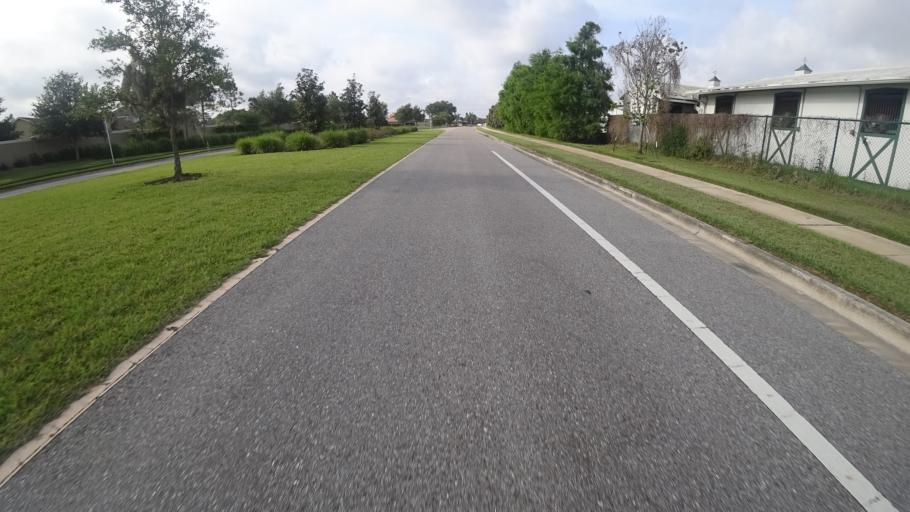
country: US
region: Florida
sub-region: Sarasota County
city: North Sarasota
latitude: 27.4157
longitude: -82.5134
